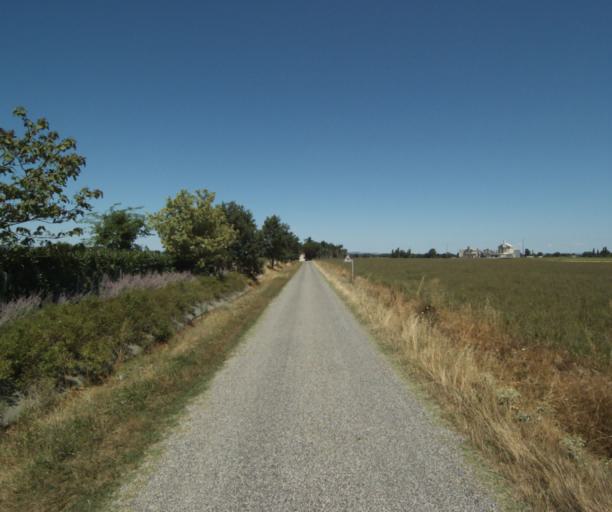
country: FR
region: Midi-Pyrenees
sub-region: Departement de la Haute-Garonne
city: Revel
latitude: 43.4468
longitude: 1.9494
